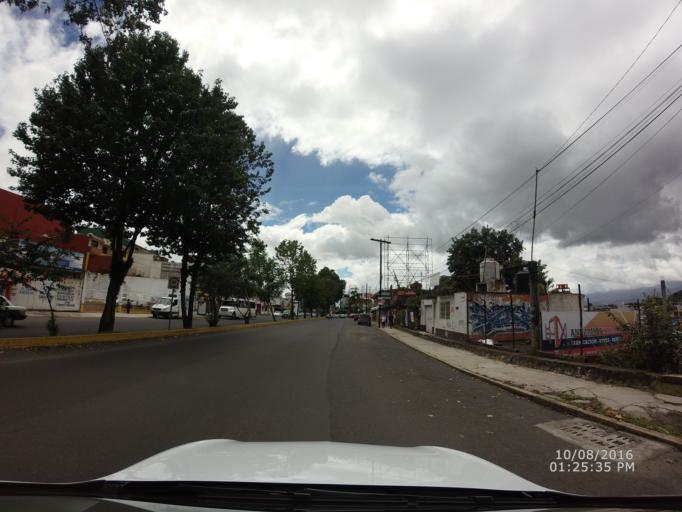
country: MX
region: Veracruz
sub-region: Xalapa
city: Xalapa de Enriquez
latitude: 19.5442
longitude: -96.9339
